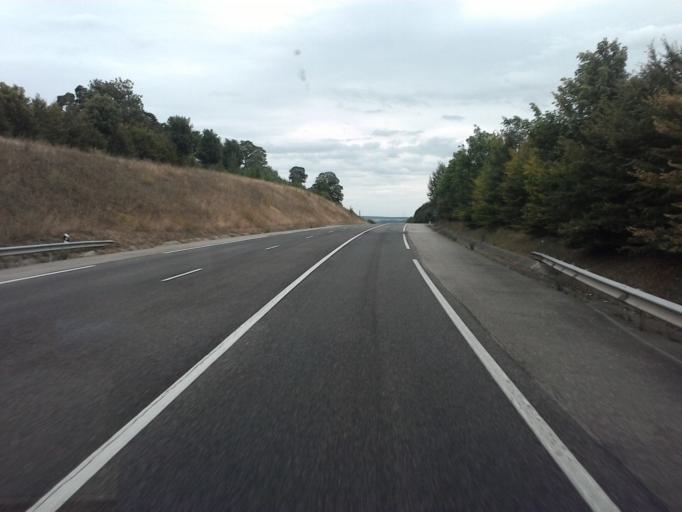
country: FR
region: Lorraine
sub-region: Departement de Meurthe-et-Moselle
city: Bainville-sur-Madon
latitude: 48.5806
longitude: 6.0268
